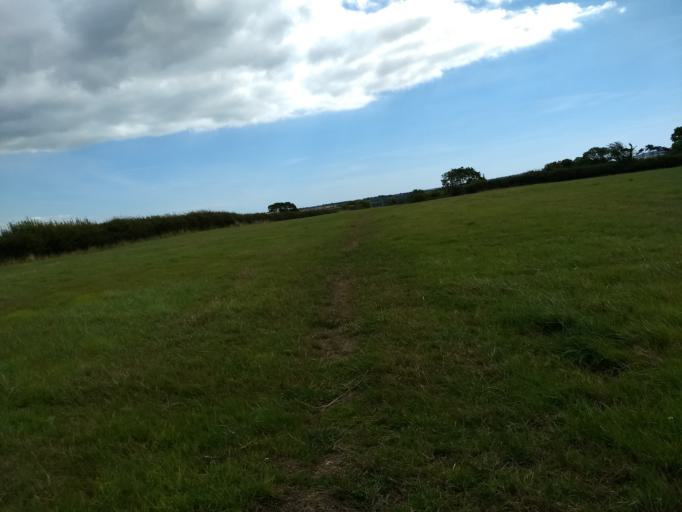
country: GB
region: England
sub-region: Isle of Wight
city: Ryde
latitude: 50.7080
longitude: -1.1846
